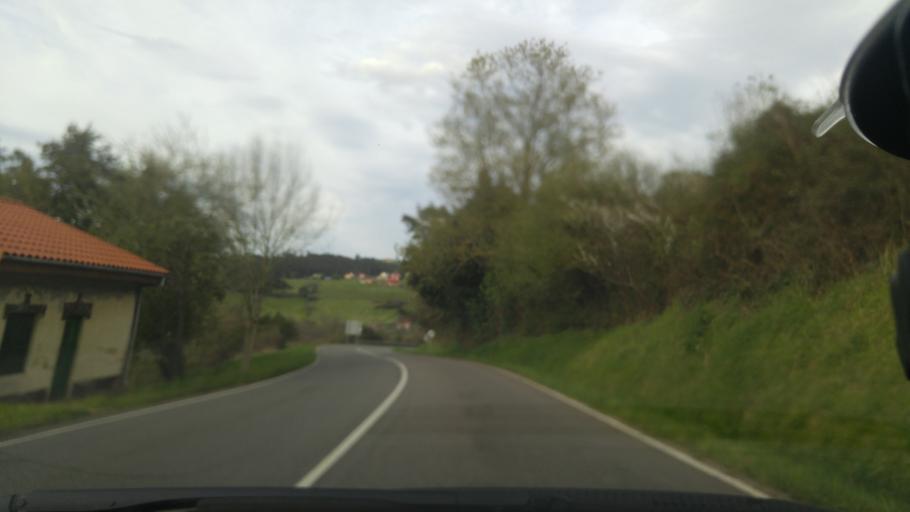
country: ES
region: Asturias
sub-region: Province of Asturias
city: Corvera de Asturias
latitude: 43.4841
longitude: -5.8490
